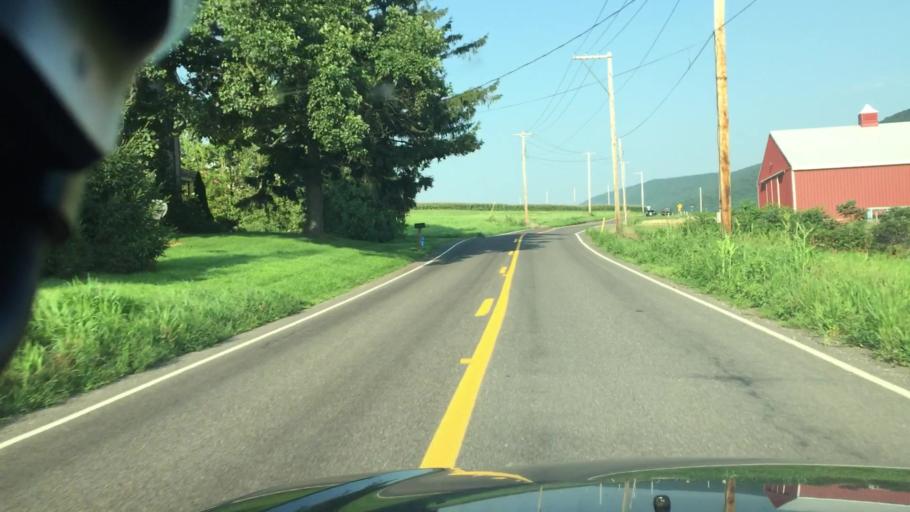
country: US
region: Pennsylvania
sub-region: Columbia County
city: Almedia
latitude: 40.9911
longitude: -76.3448
